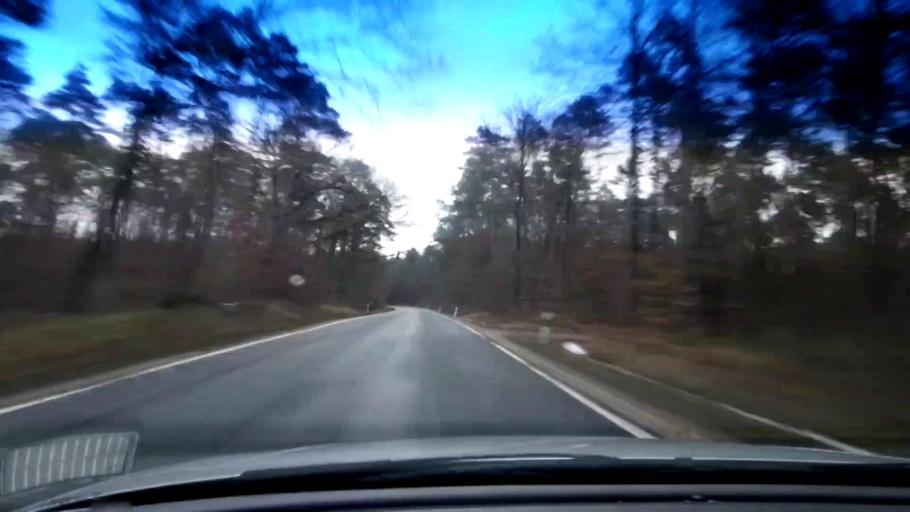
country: DE
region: Bavaria
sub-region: Upper Franconia
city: Walsdorf
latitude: 49.8663
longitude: 10.7493
